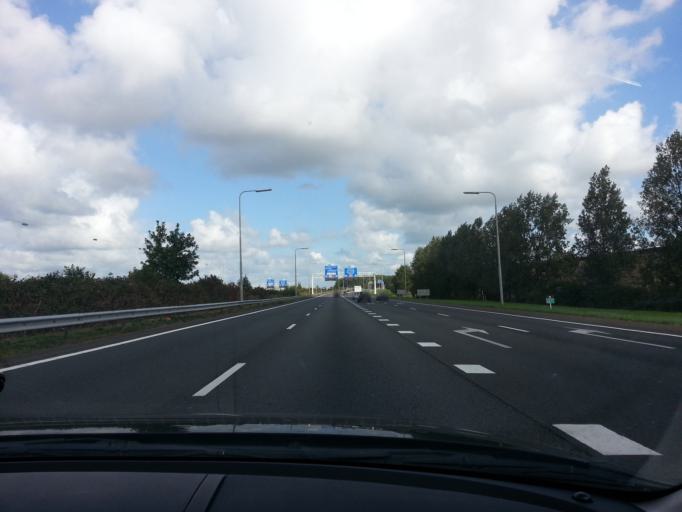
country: NL
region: South Holland
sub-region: Gemeente Den Haag
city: Ypenburg
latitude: 52.0486
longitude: 4.3602
